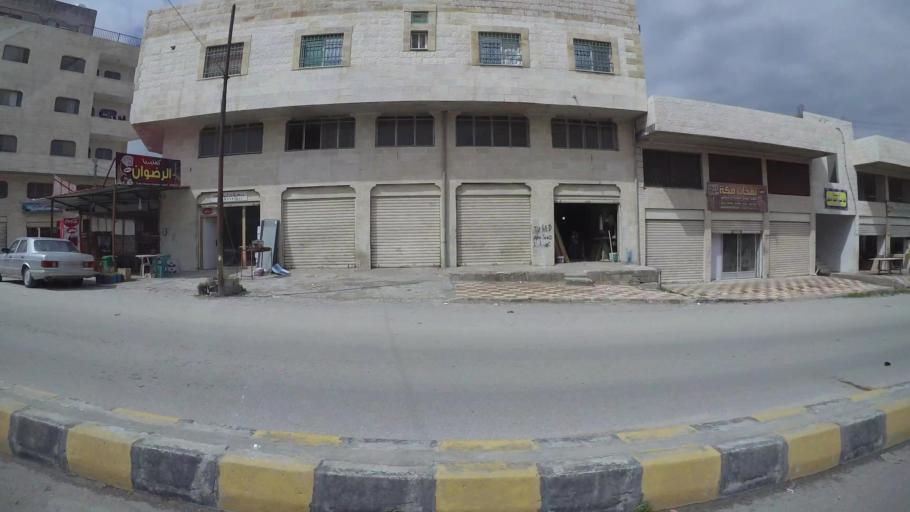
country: JO
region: Amman
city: Al Jubayhah
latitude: 32.0529
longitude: 35.8293
